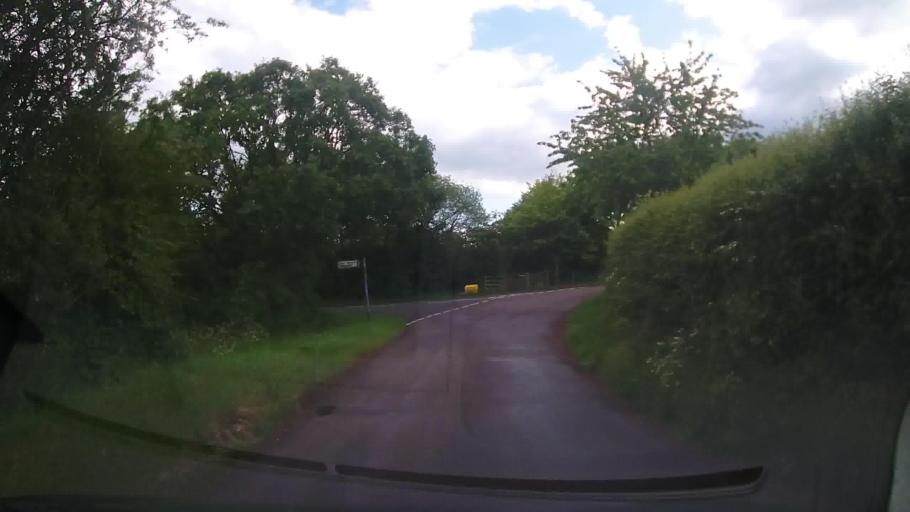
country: GB
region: England
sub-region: Telford and Wrekin
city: Wellington
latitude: 52.6576
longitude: -2.5189
